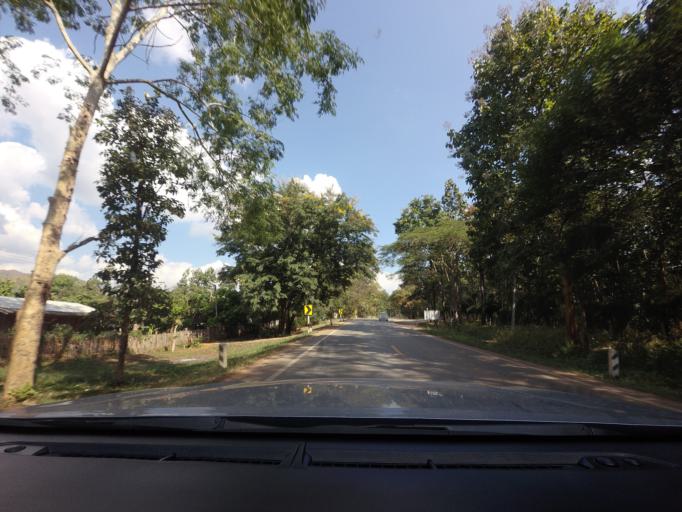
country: TH
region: Chiang Mai
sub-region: Amphoe Chiang Dao
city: Chiang Dao
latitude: 19.4906
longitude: 99.0295
